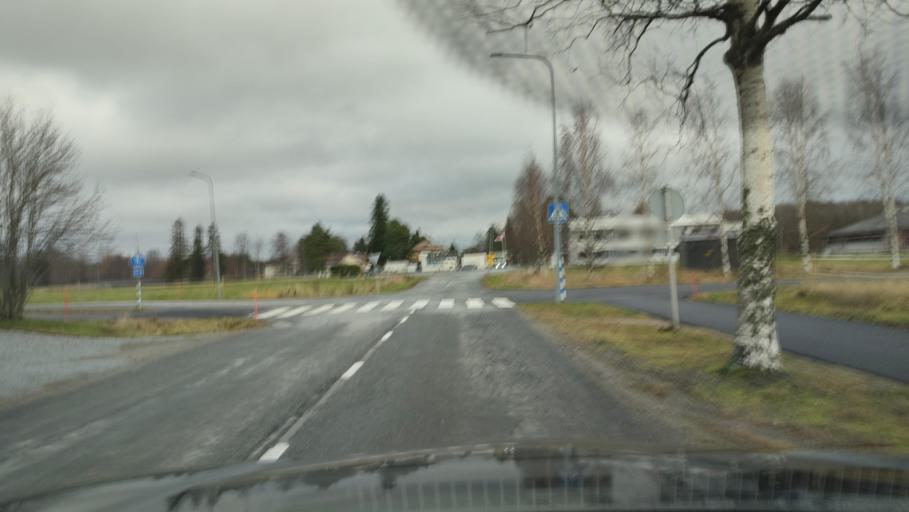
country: FI
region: Southern Ostrobothnia
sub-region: Suupohja
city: Kauhajoki
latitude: 62.4157
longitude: 22.1847
